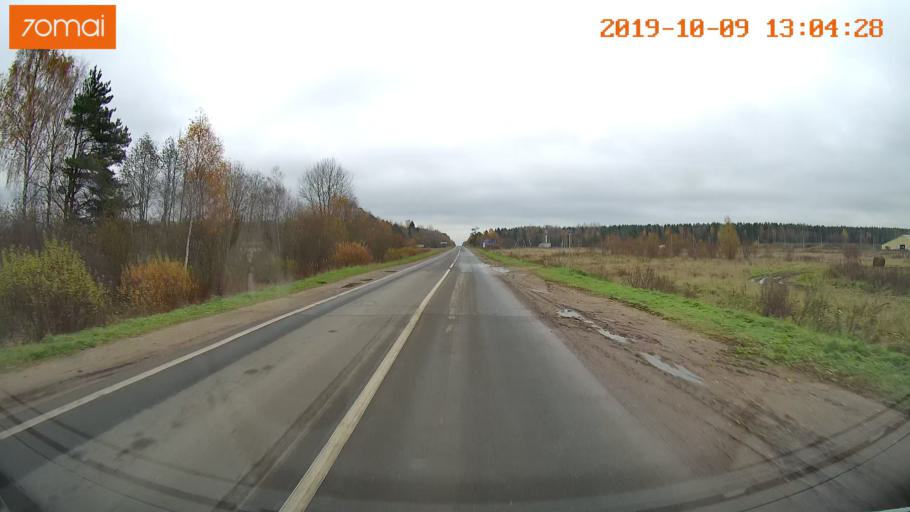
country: RU
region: Jaroslavl
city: Lyubim
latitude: 58.3584
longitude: 40.5548
